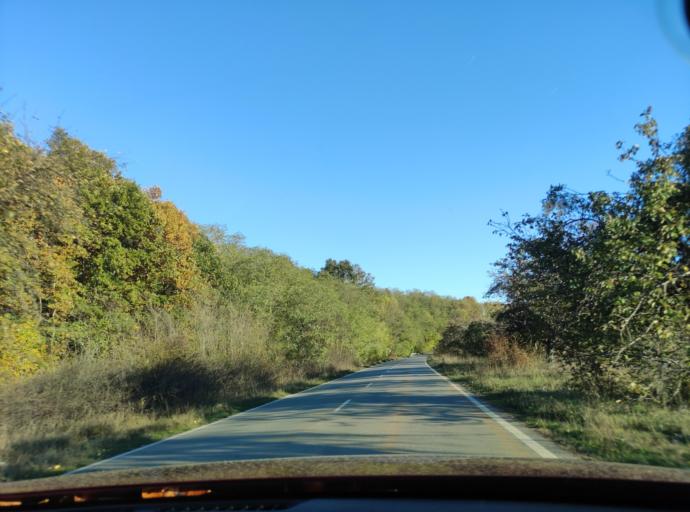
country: BG
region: Montana
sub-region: Obshtina Chiprovtsi
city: Chiprovtsi
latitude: 43.4094
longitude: 23.0496
